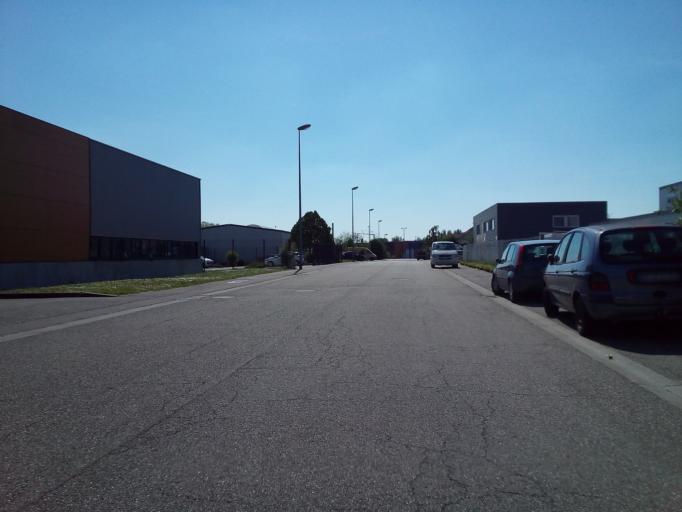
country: FR
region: Alsace
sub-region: Departement du Bas-Rhin
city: Hoenheim
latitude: 48.6325
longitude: 7.7663
